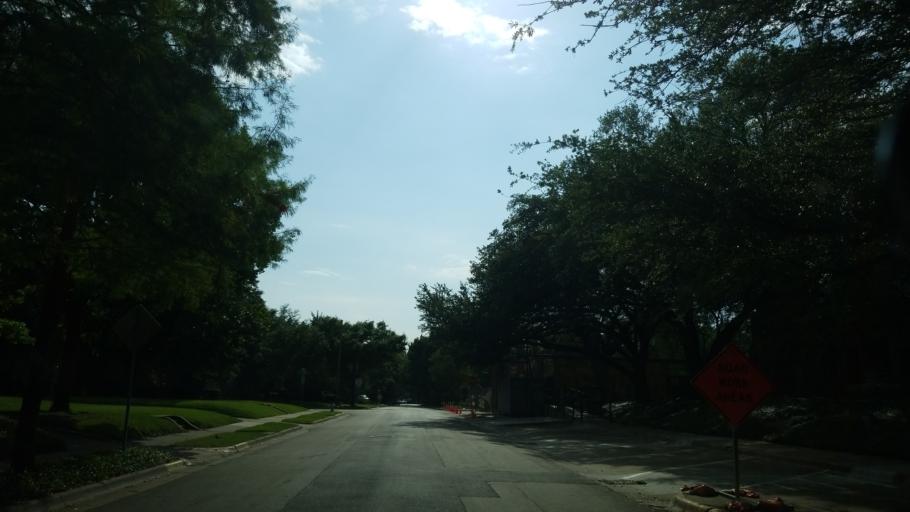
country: US
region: Texas
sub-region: Dallas County
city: University Park
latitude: 32.8441
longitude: -96.7996
